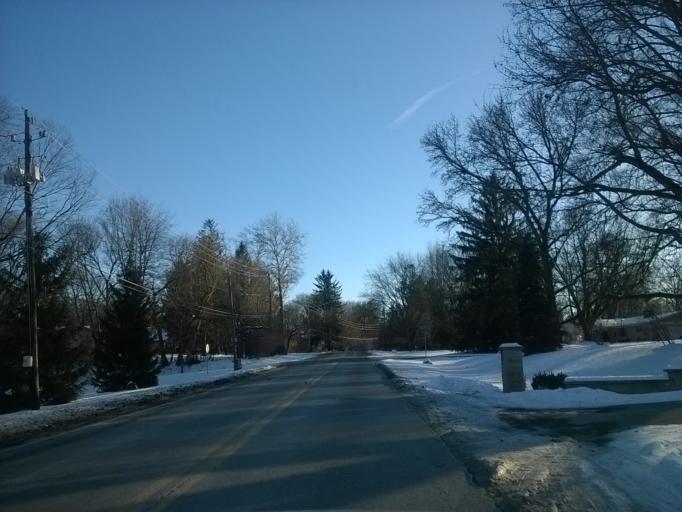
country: US
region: Indiana
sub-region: Marion County
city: Meridian Hills
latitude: 39.8984
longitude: -86.1364
